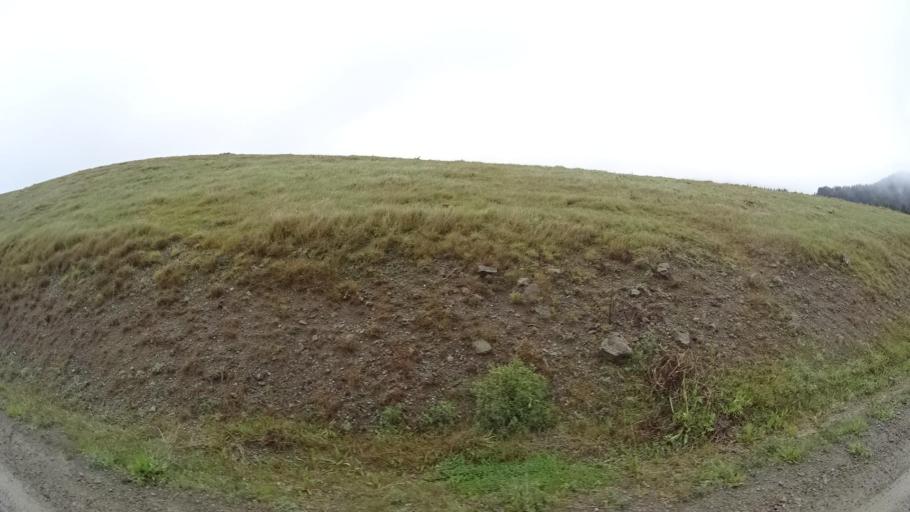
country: US
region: California
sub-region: Humboldt County
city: Westhaven-Moonstone
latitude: 41.1447
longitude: -123.8678
